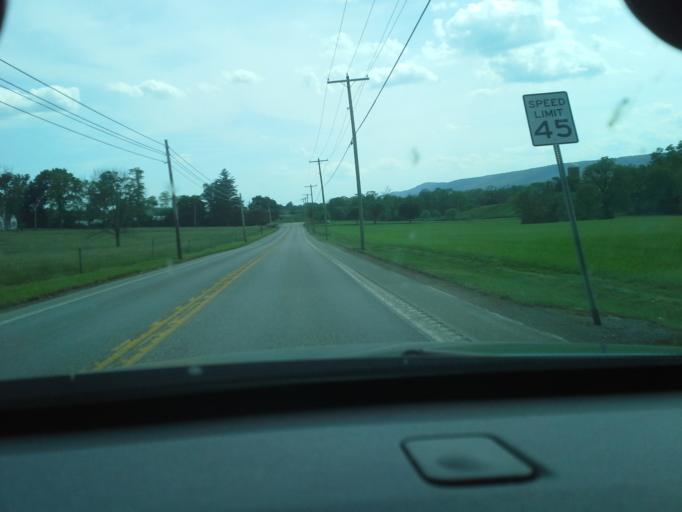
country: US
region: Pennsylvania
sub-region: Fulton County
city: McConnellsburg
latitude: 39.9484
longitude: -77.9900
